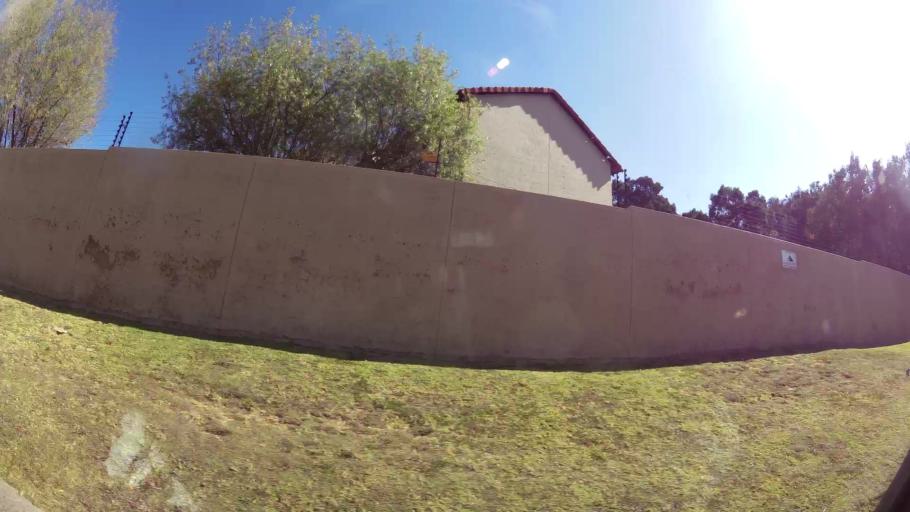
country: ZA
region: Gauteng
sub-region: City of Johannesburg Metropolitan Municipality
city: Johannesburg
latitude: -26.2641
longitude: 27.9872
